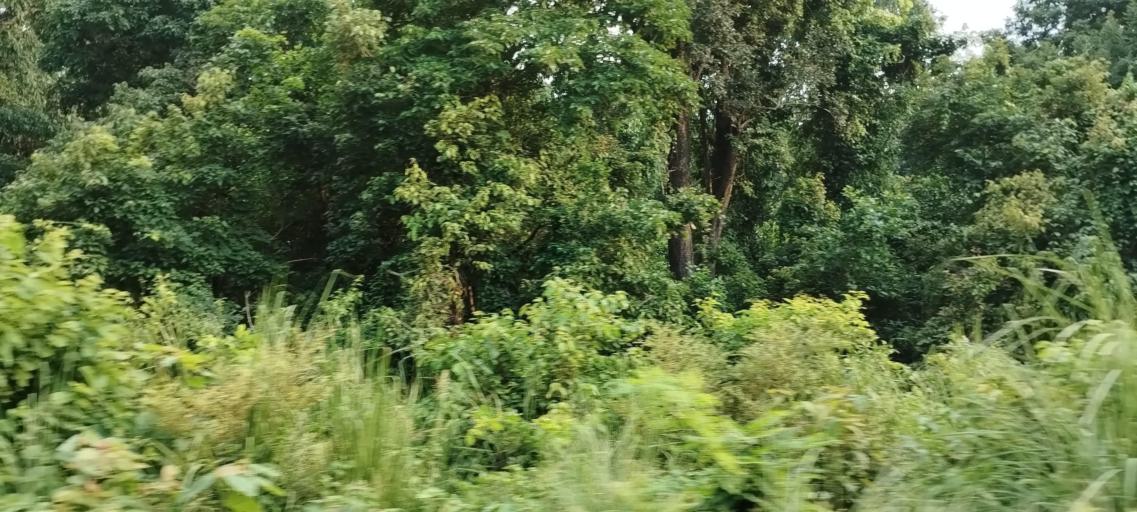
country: NP
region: Mid Western
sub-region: Bheri Zone
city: Bardiya
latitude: 28.4299
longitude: 81.3477
